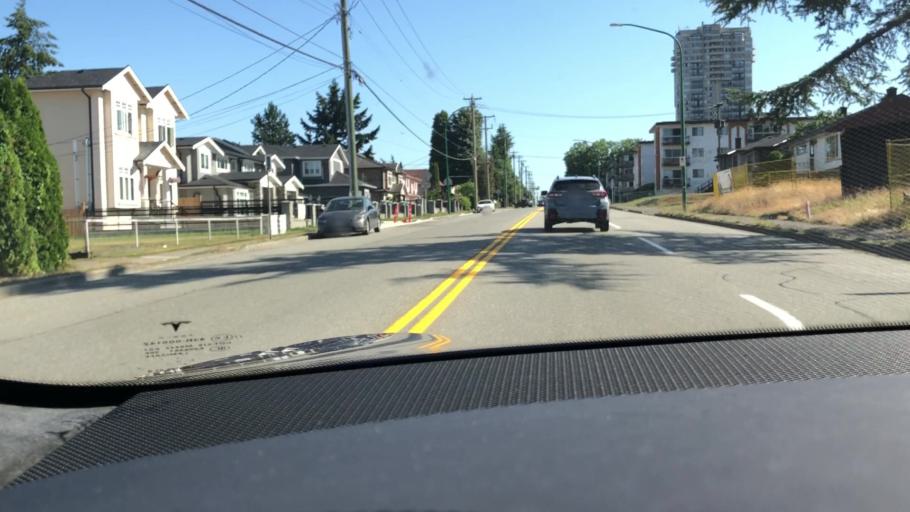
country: CA
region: British Columbia
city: Burnaby
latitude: 49.2278
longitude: -122.9890
